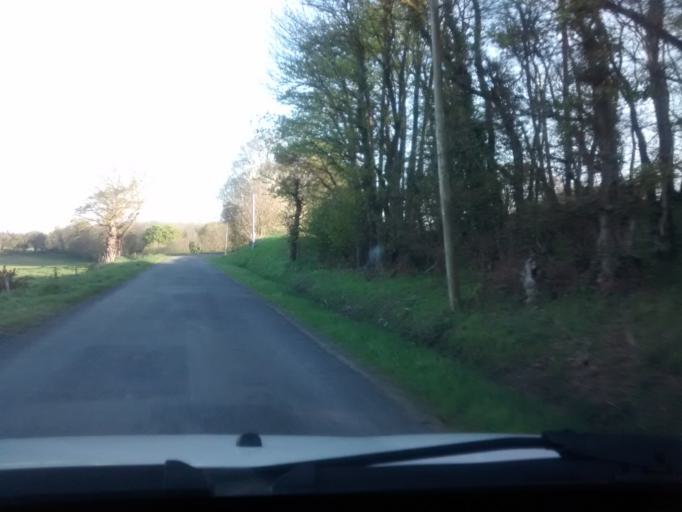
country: FR
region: Brittany
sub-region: Departement d'Ille-et-Vilaine
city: Saint-Broladre
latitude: 48.5716
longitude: -1.6444
